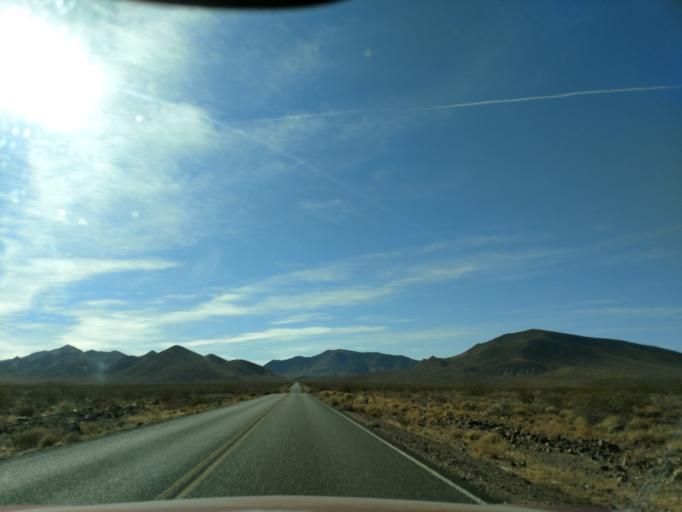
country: US
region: Nevada
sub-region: Nye County
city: Beatty
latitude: 36.8214
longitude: -116.8942
